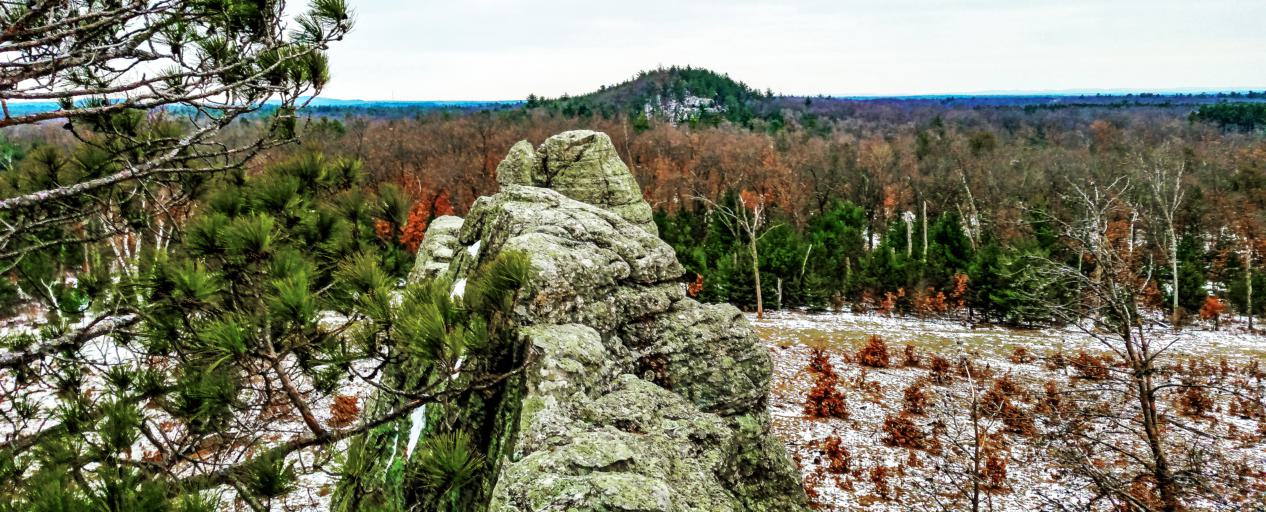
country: US
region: Wisconsin
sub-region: Adams County
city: Adams
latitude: 43.8737
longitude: -89.8391
